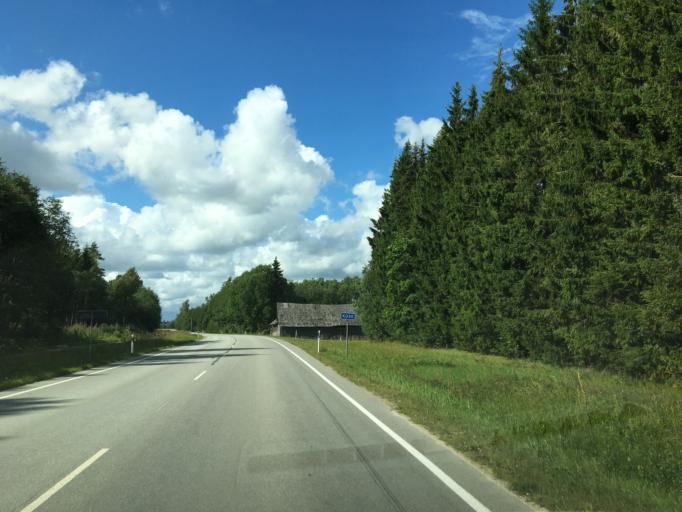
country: EE
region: Paernumaa
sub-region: Vaendra vald (alev)
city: Vandra
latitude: 58.6247
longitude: 25.1056
